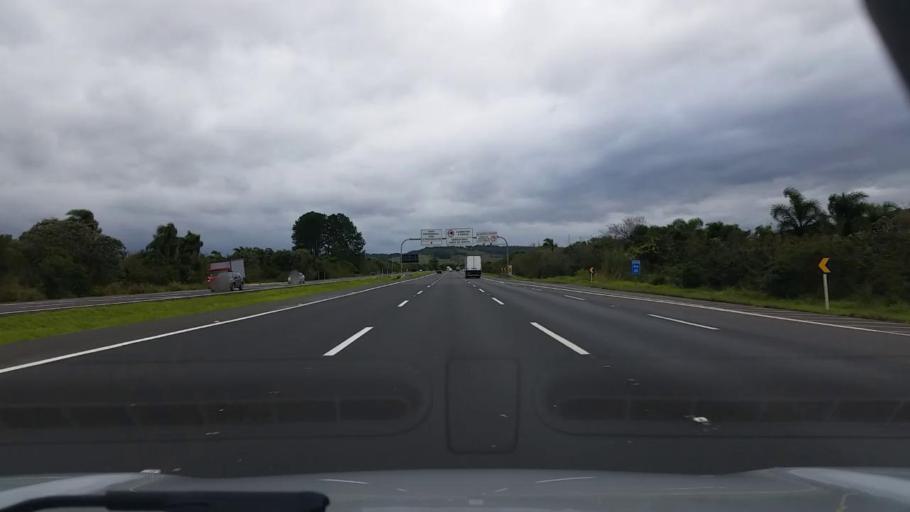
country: BR
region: Rio Grande do Sul
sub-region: Osorio
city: Osorio
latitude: -29.8871
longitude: -50.4535
